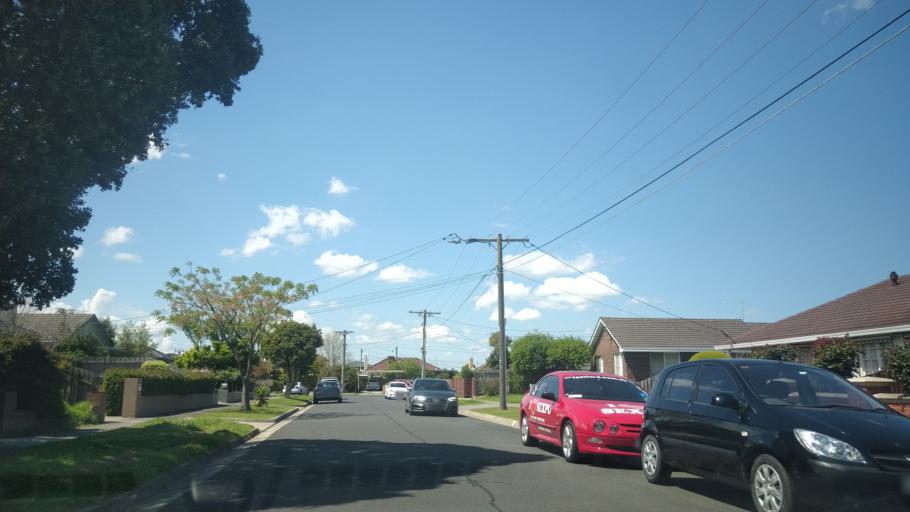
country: AU
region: Victoria
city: Highett
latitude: -37.9530
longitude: 145.0564
